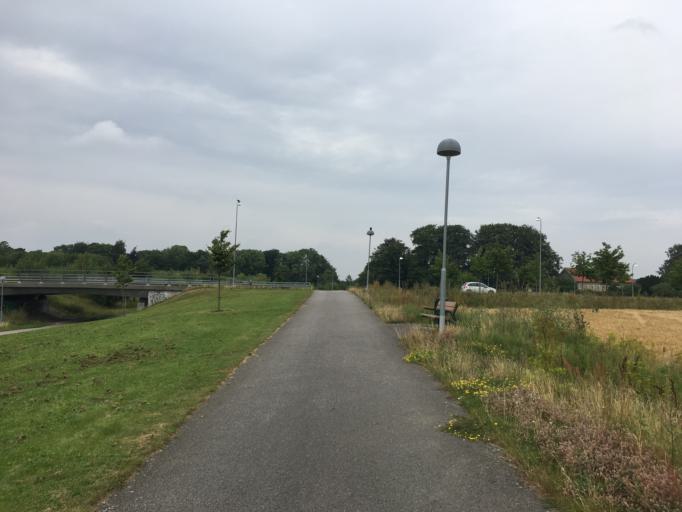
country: SE
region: Skane
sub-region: Lunds Kommun
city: Lund
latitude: 55.6838
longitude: 13.2068
